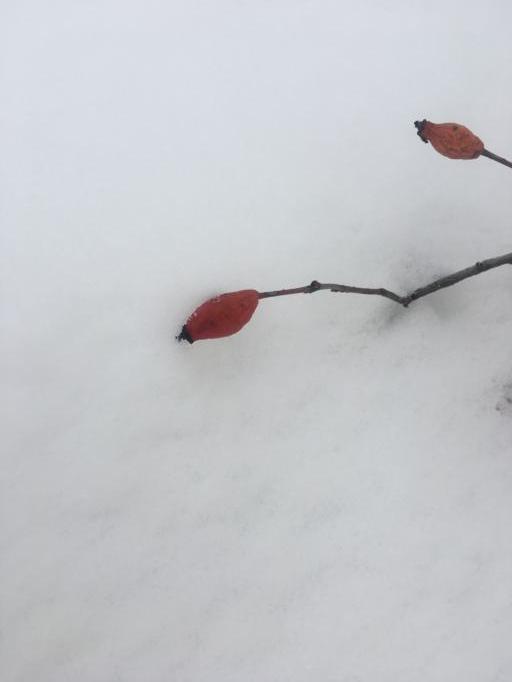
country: XK
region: Pristina
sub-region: Komuna e Drenasit
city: Glogovac
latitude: 42.6410
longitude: 20.9048
